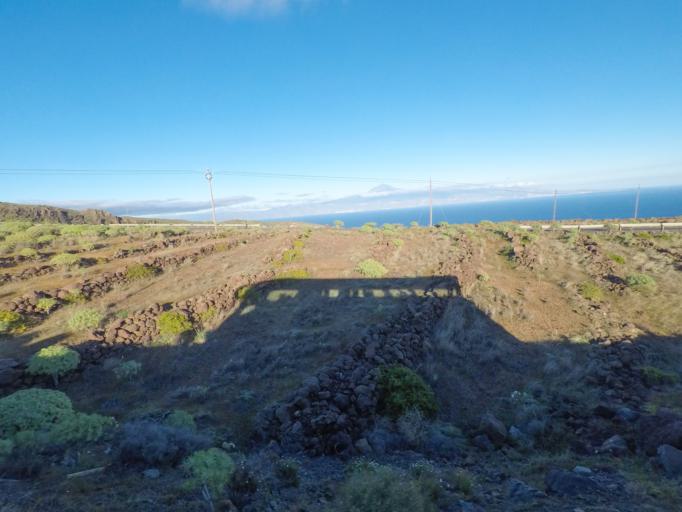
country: ES
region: Canary Islands
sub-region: Provincia de Santa Cruz de Tenerife
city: San Sebastian de la Gomera
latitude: 28.0873
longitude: -17.1467
